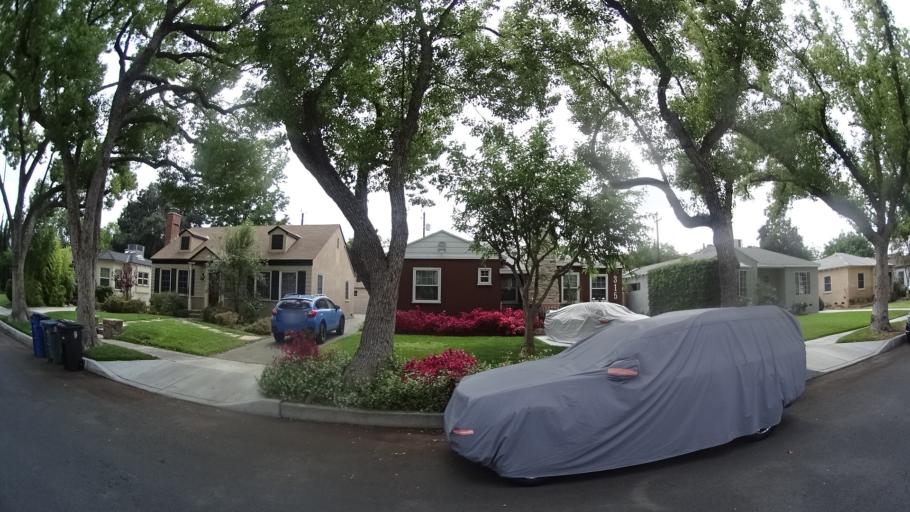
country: US
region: California
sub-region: Los Angeles County
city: Burbank
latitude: 34.1697
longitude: -118.3253
